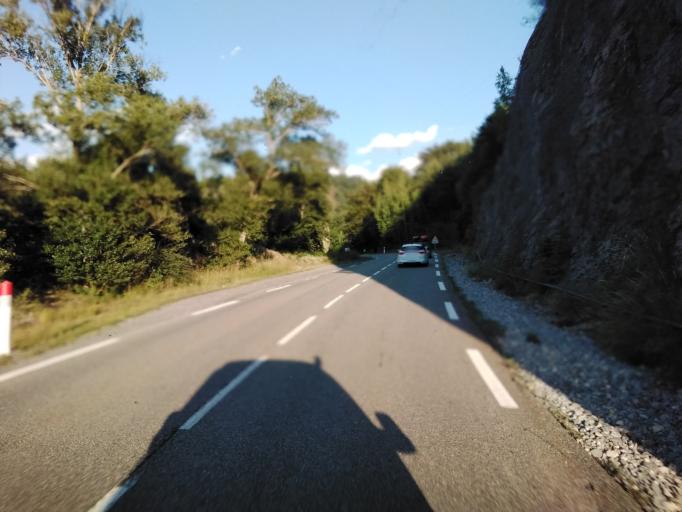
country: FR
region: Provence-Alpes-Cote d'Azur
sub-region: Departement des Hautes-Alpes
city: Chorges
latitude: 44.4622
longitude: 6.2722
